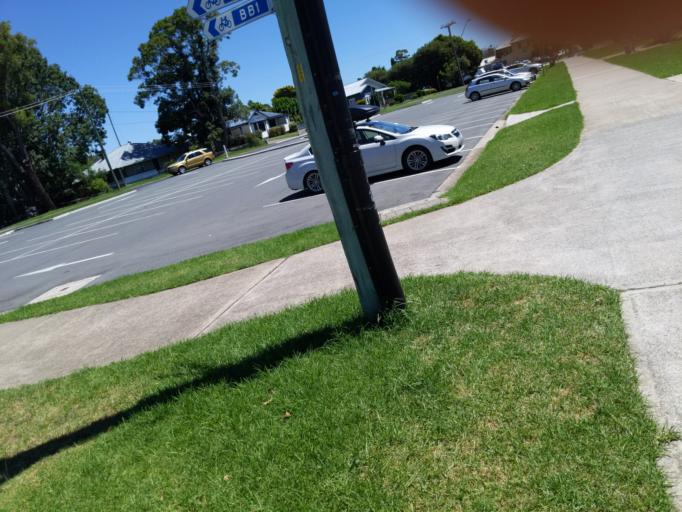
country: AU
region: New South Wales
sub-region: Eurobodalla
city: Moruya
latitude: -35.9085
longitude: 150.0835
